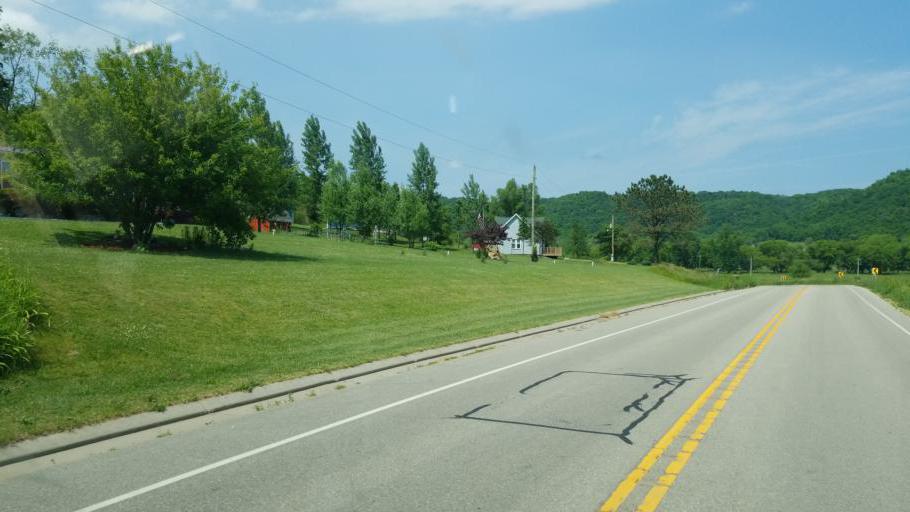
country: US
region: Wisconsin
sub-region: Vernon County
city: Viroqua
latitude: 43.5300
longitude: -90.6645
